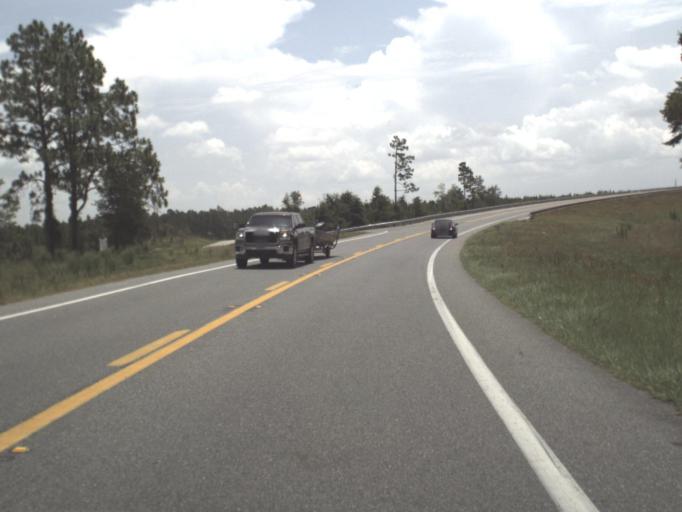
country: US
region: Florida
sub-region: Madison County
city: Madison
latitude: 30.4006
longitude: -83.2097
